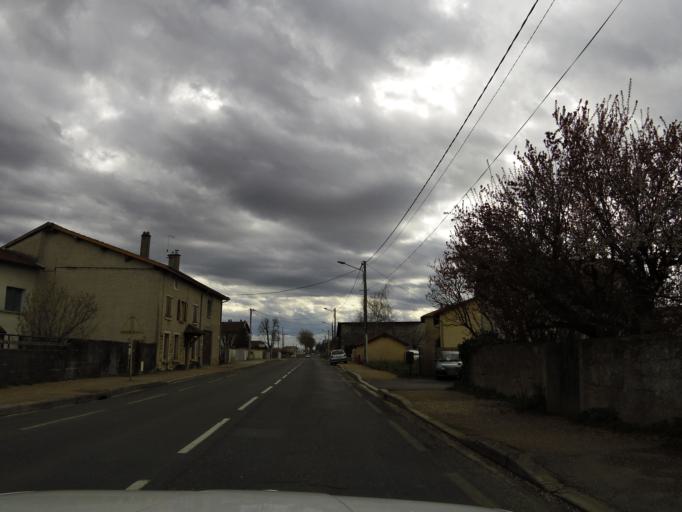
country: FR
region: Rhone-Alpes
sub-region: Departement de l'Ain
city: Meximieux
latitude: 45.9186
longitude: 5.2216
